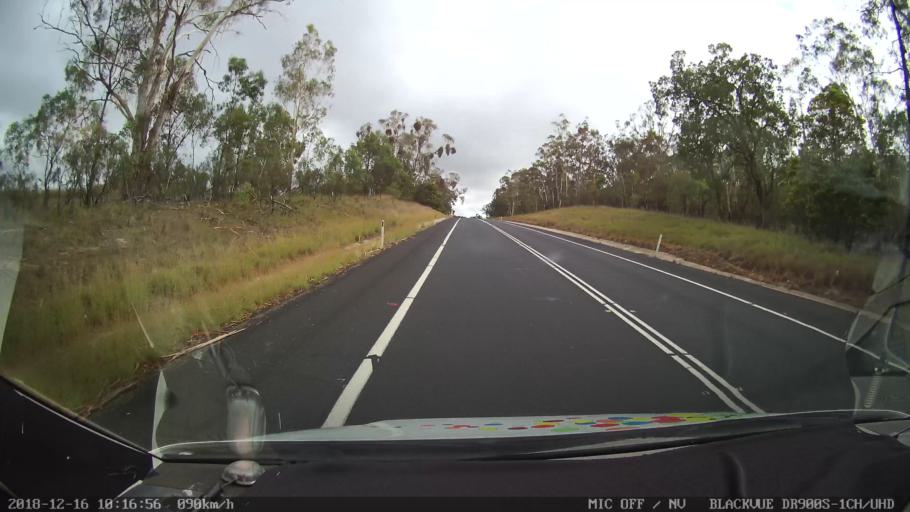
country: AU
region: New South Wales
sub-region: Tenterfield Municipality
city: Carrolls Creek
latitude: -29.2617
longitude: 151.9877
